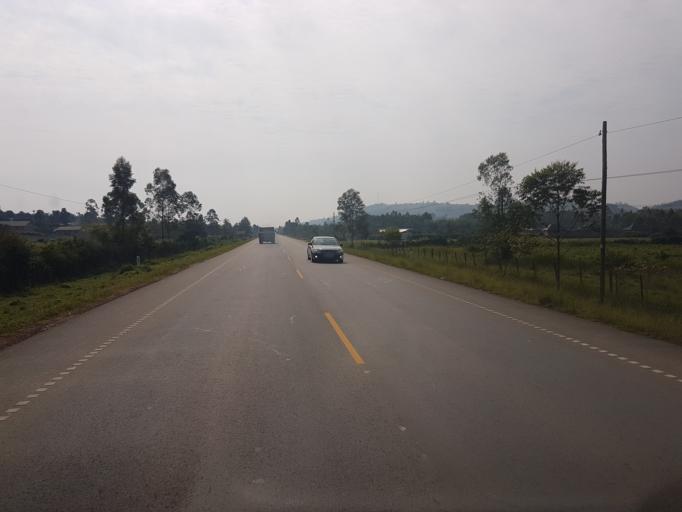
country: UG
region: Western Region
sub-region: Sheema District
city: Kibingo
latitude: -0.6462
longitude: 30.4927
